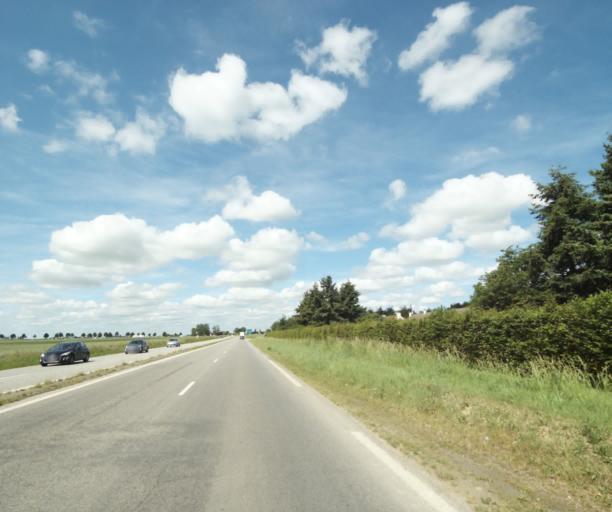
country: FR
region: Centre
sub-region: Departement d'Eure-et-Loir
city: Mainvilliers
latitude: 48.4368
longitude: 1.4393
